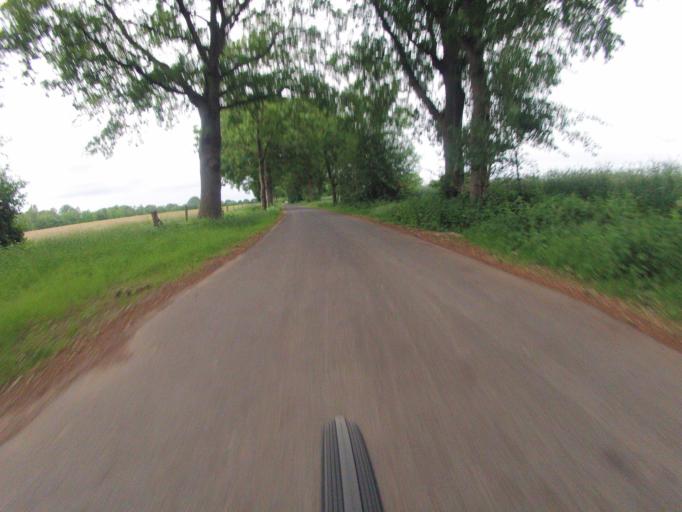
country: DE
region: North Rhine-Westphalia
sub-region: Regierungsbezirk Munster
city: Horstel
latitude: 52.2605
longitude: 7.5713
